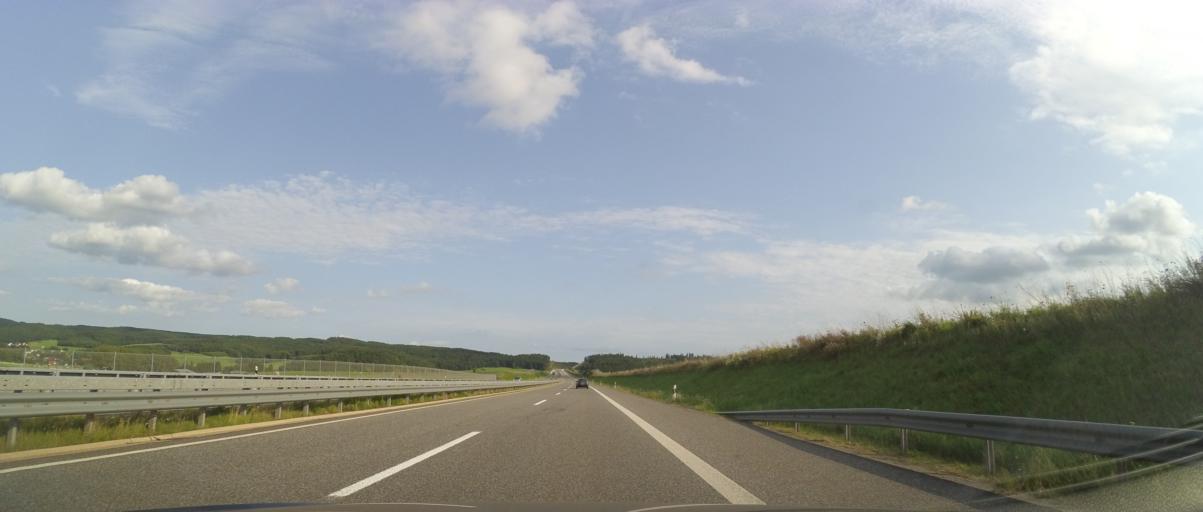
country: DE
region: Rheinland-Pfalz
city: Kradenbach
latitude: 50.2349
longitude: 6.8413
